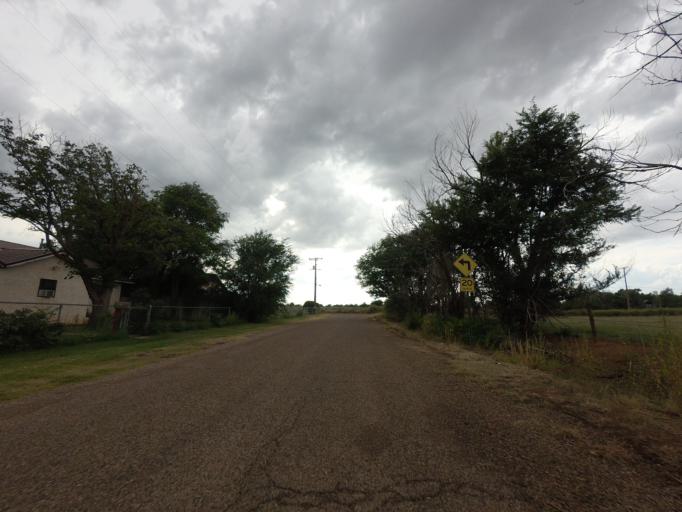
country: US
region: New Mexico
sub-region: Curry County
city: Clovis
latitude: 34.3878
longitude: -103.1868
